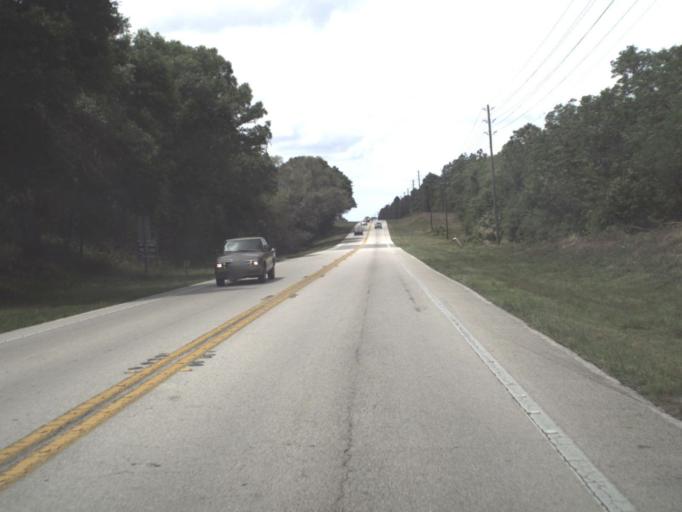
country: US
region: Florida
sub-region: Lake County
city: Mount Dora
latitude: 28.8517
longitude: -81.6036
